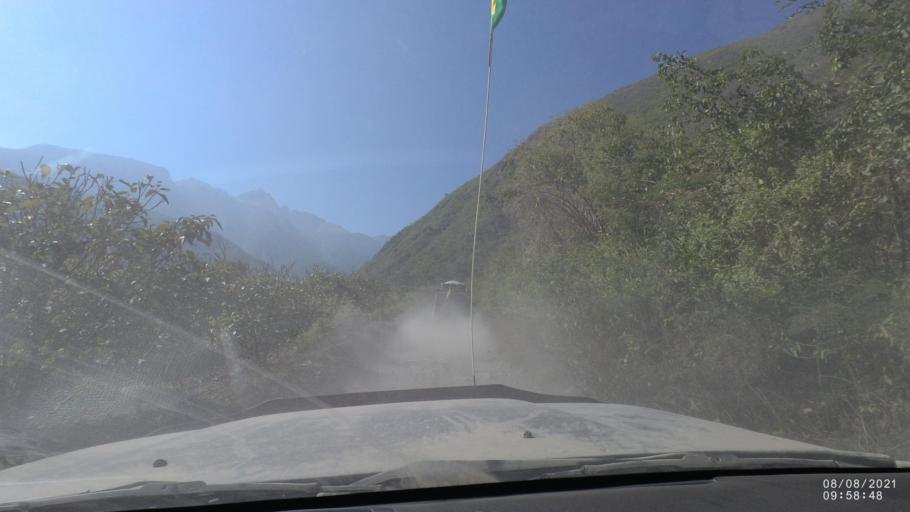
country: BO
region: La Paz
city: Quime
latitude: -16.6448
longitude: -66.7237
